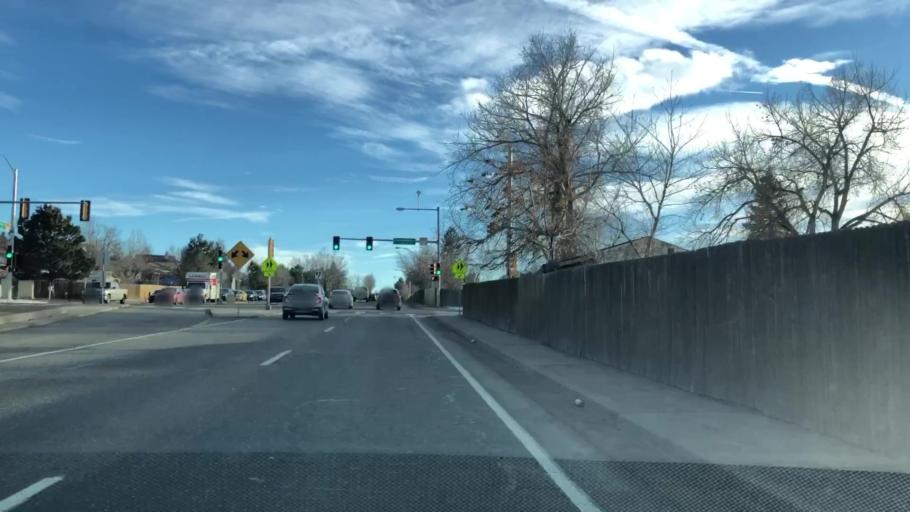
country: US
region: Colorado
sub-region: Adams County
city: Aurora
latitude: 39.6610
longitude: -104.7914
